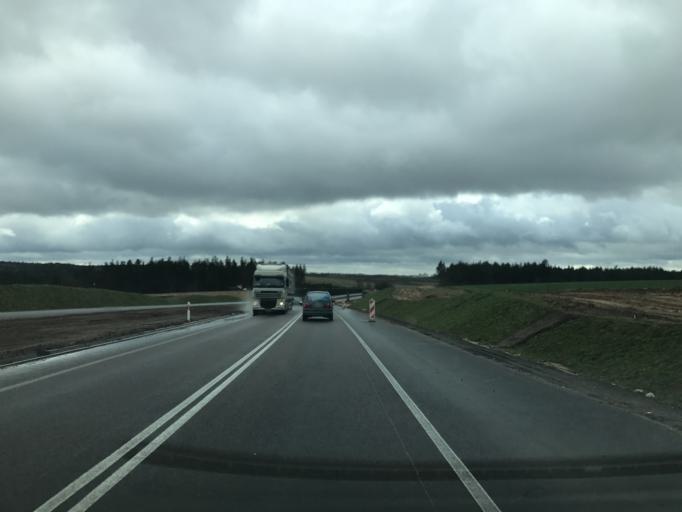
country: PL
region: Warmian-Masurian Voivodeship
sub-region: Powiat olsztynski
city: Olsztynek
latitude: 53.6183
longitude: 20.3355
